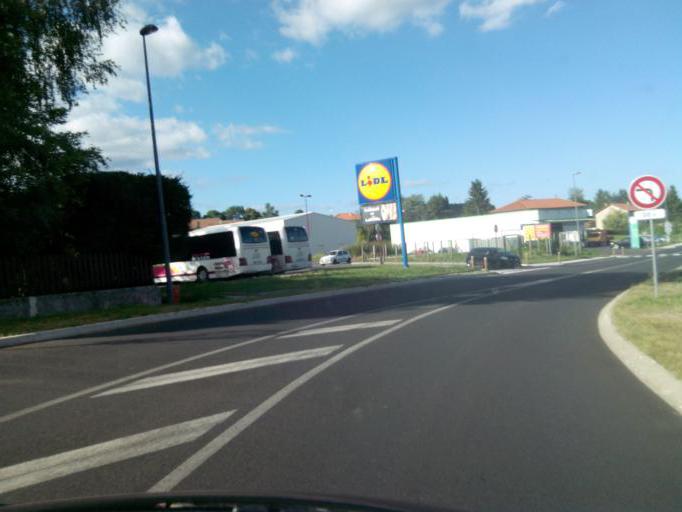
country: FR
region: Auvergne
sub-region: Departement de la Haute-Loire
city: Craponne-sur-Arzon
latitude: 45.3345
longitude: 3.8528
